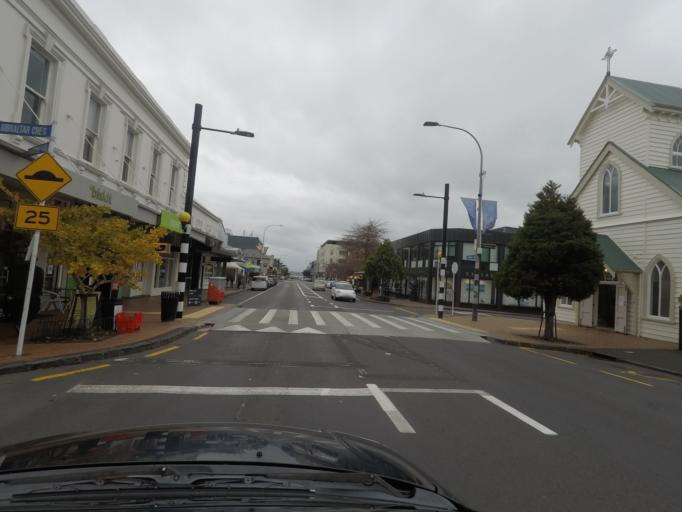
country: NZ
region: Auckland
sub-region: Auckland
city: Auckland
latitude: -36.8552
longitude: 174.7803
